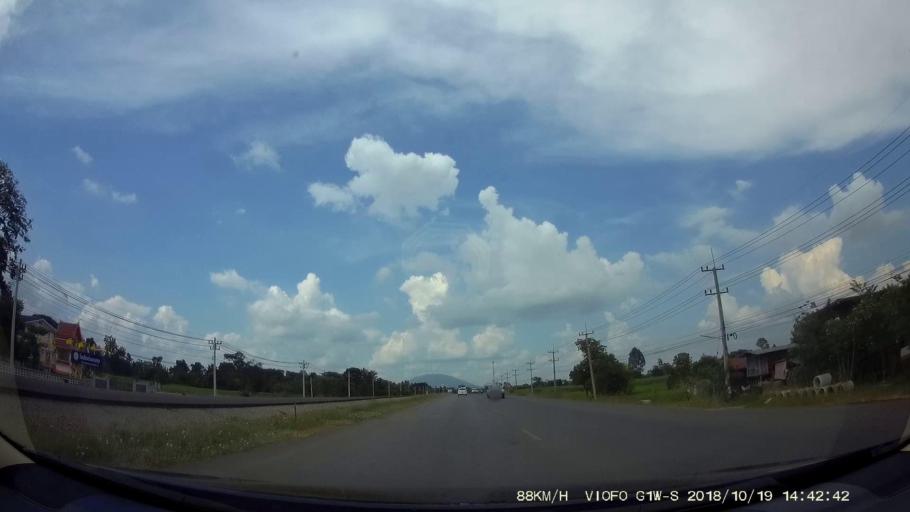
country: TH
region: Chaiyaphum
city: Phu Khiao
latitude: 16.2715
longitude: 102.2038
